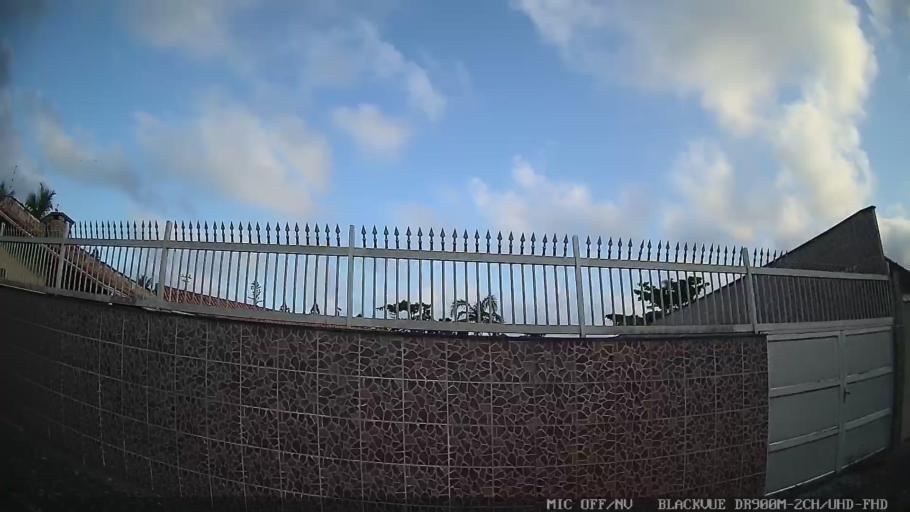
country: BR
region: Sao Paulo
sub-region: Peruibe
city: Peruibe
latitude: -24.3190
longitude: -46.9899
